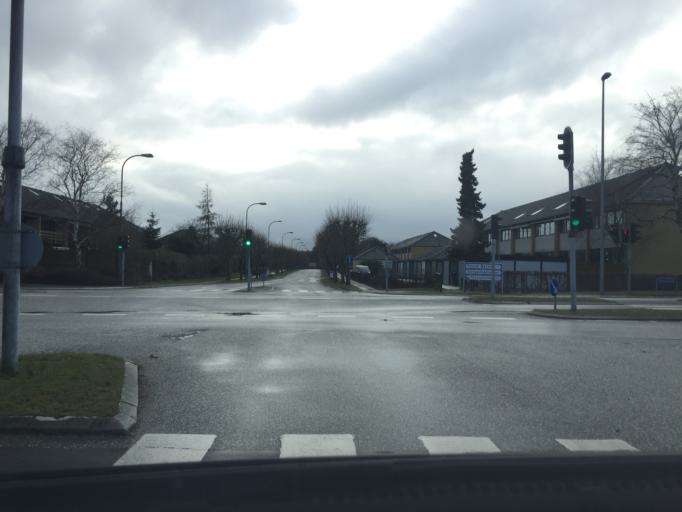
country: DK
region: Capital Region
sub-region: Fureso Kommune
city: Stavnsholt
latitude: 55.8135
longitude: 12.3886
